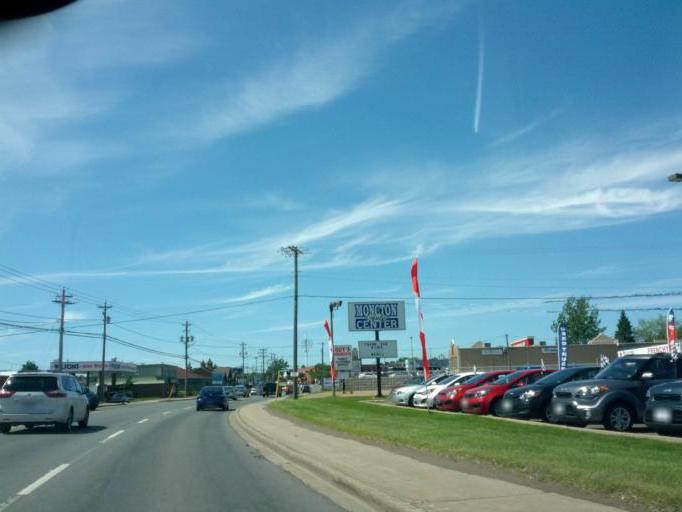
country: CA
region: New Brunswick
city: Moncton
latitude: 46.1151
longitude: -64.8383
